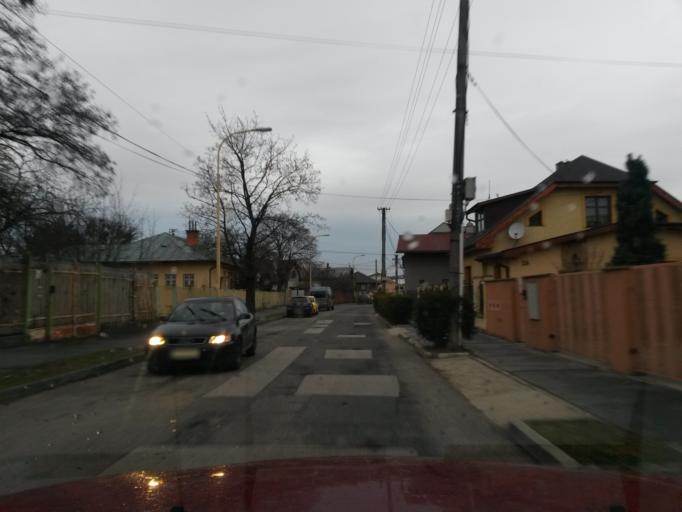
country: SK
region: Kosicky
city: Kosice
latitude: 48.7368
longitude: 21.2688
